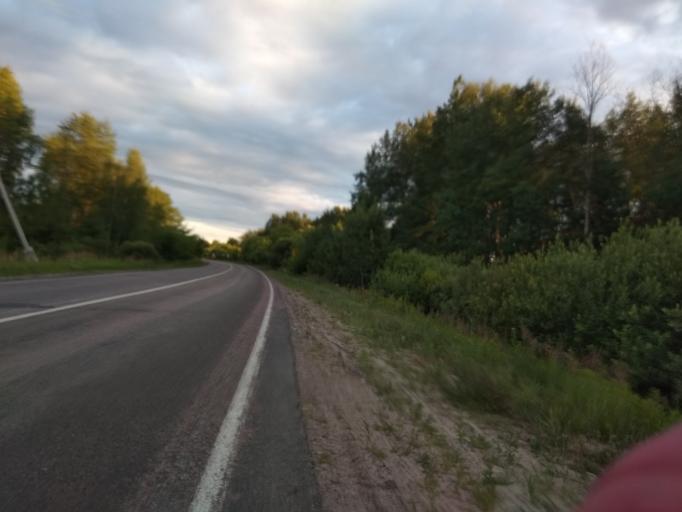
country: RU
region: Moskovskaya
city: Misheronskiy
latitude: 55.6048
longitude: 39.7088
